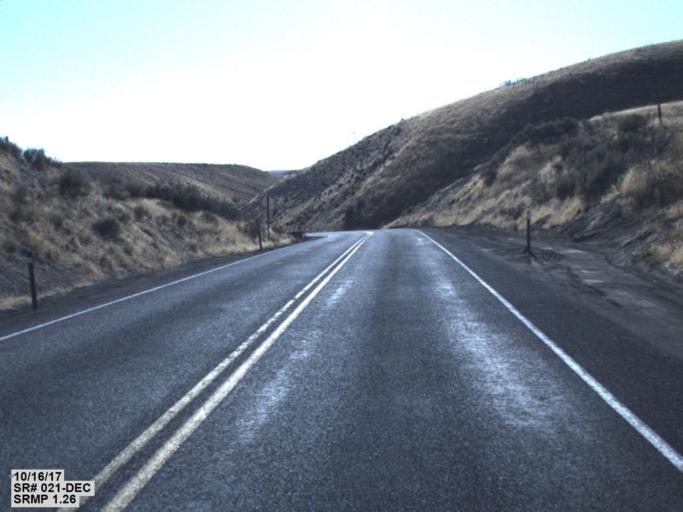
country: US
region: Washington
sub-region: Franklin County
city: Connell
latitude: 46.6592
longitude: -118.5483
